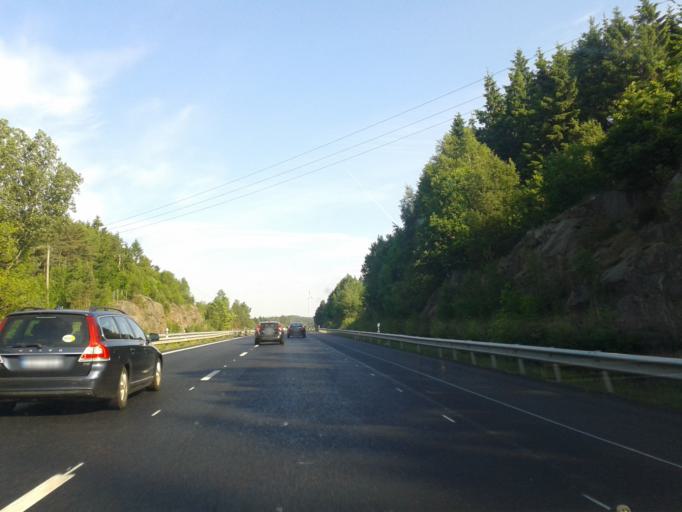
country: SE
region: Vaestra Goetaland
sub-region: Kungalvs Kommun
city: Kode
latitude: 57.9089
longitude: 11.8984
